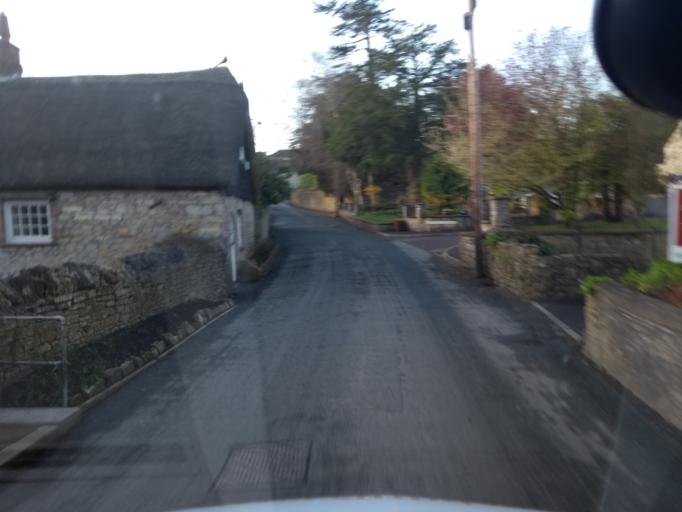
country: GB
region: England
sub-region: Somerset
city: Wedmore
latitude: 51.2268
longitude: -2.8116
